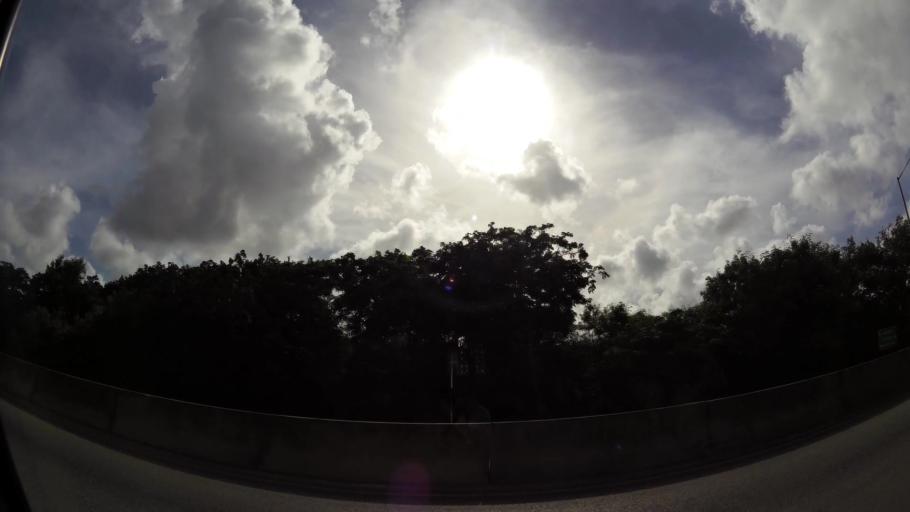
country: BB
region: Saint Michael
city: Bridgetown
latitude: 13.1247
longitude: -59.5935
